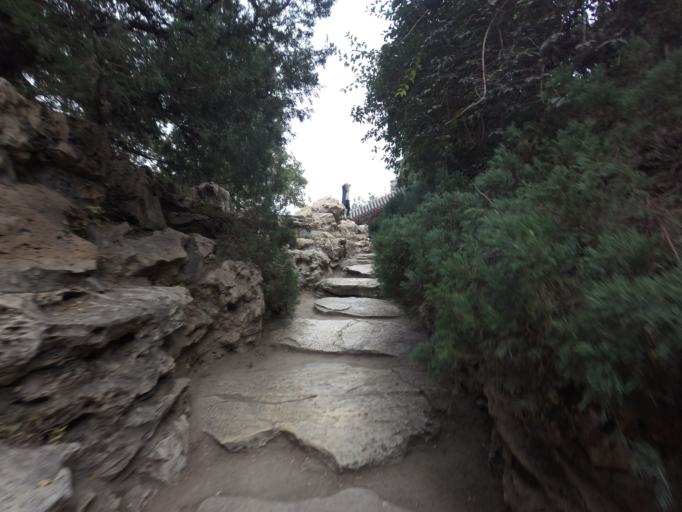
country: CN
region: Beijing
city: Jingshan
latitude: 39.9248
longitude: 116.3830
